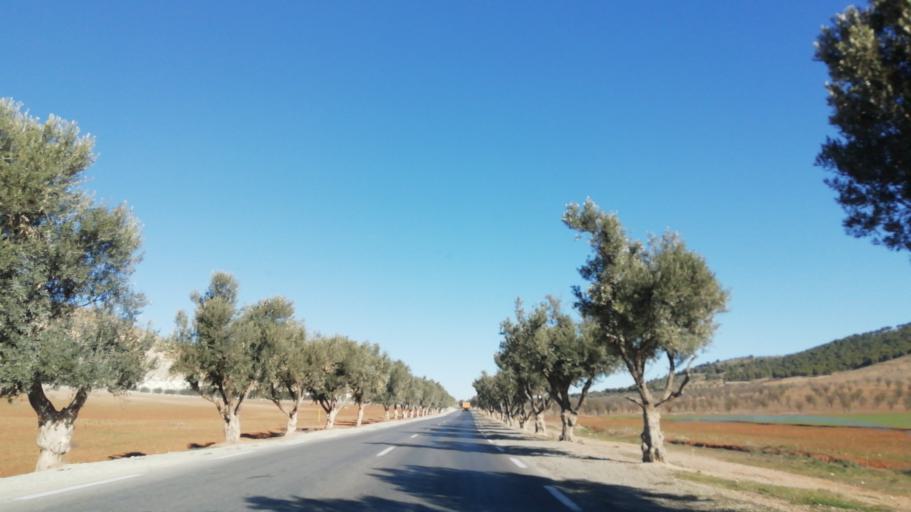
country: DZ
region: Mascara
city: Mascara
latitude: 35.2357
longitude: 0.1166
